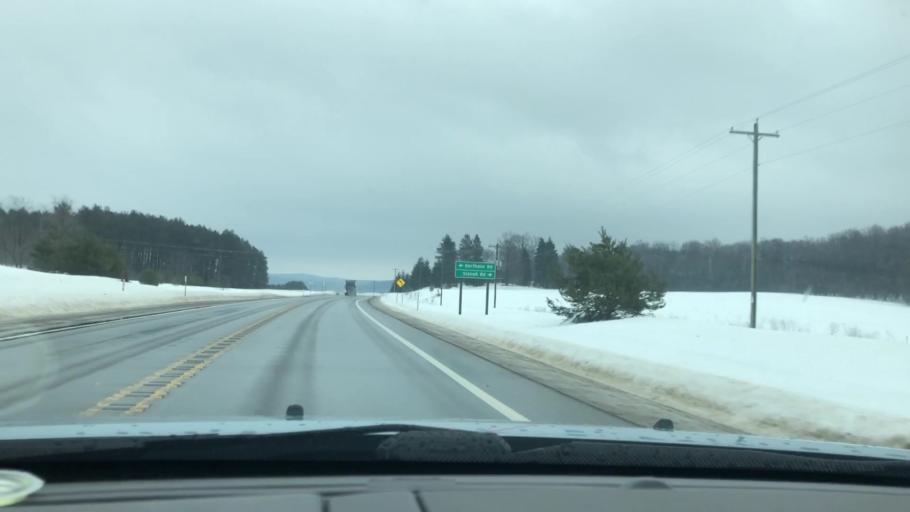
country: US
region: Michigan
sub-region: Charlevoix County
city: Boyne City
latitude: 45.0961
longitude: -84.9822
